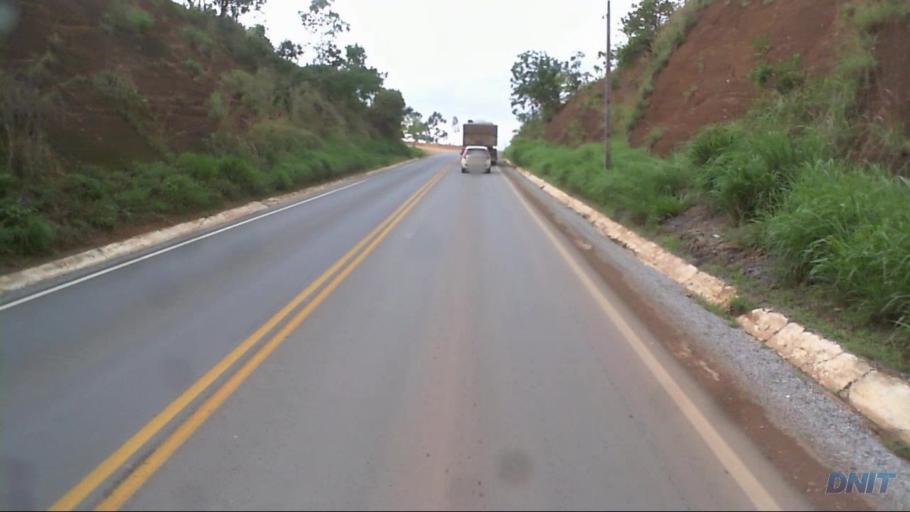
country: BR
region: Goias
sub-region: Padre Bernardo
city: Padre Bernardo
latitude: -15.1799
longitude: -48.2851
